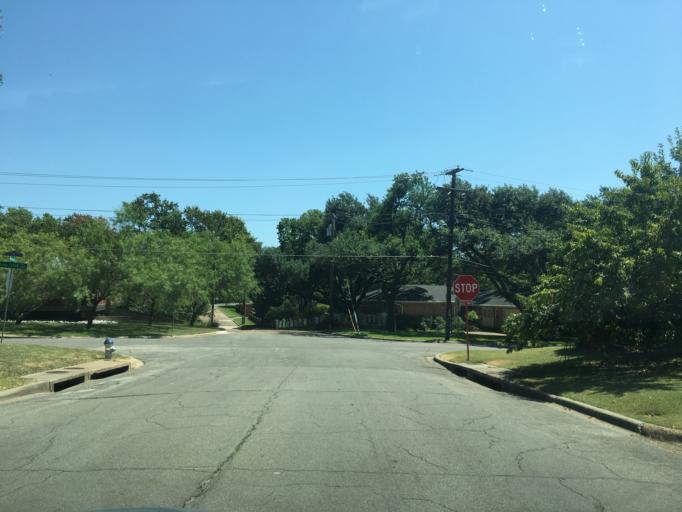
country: US
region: Texas
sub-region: Dallas County
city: Highland Park
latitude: 32.8390
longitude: -96.7490
